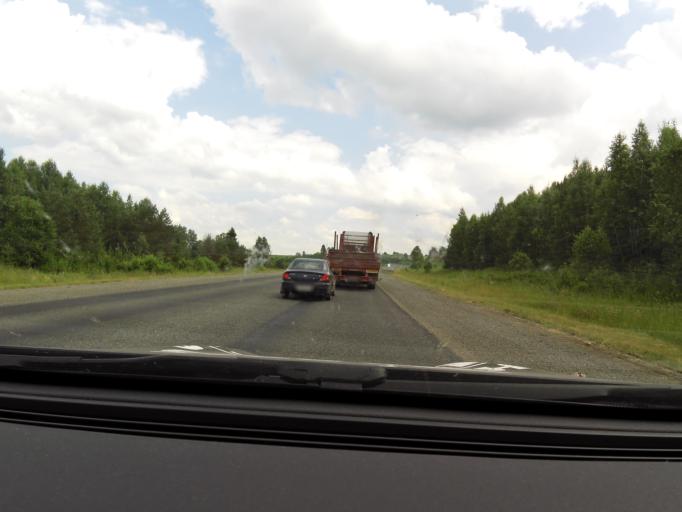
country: RU
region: Sverdlovsk
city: Ufimskiy
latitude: 56.7897
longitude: 58.3521
